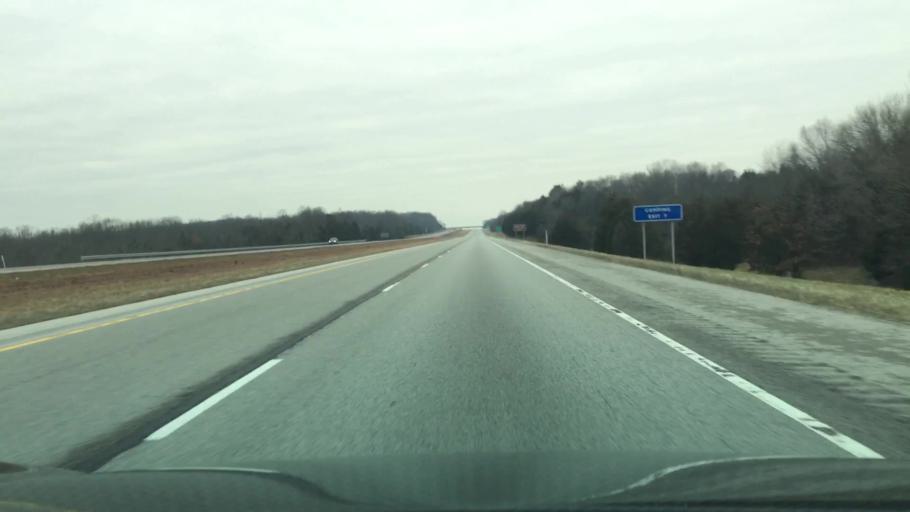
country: US
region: Illinois
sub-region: Johnson County
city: Goreville
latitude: 37.5192
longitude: -88.9127
